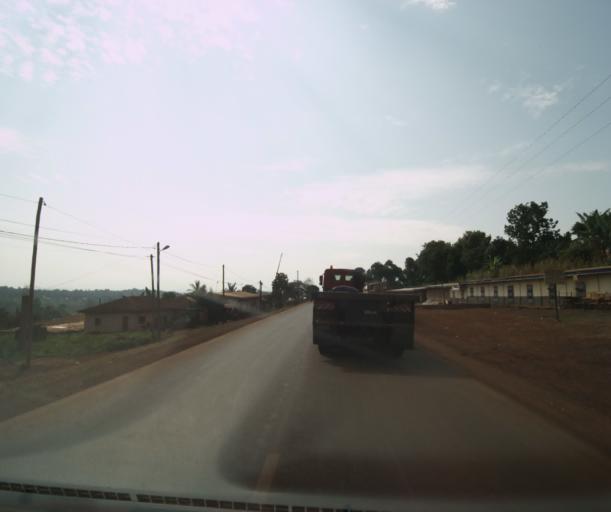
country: CM
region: West
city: Mbouda
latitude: 5.6203
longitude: 10.2693
